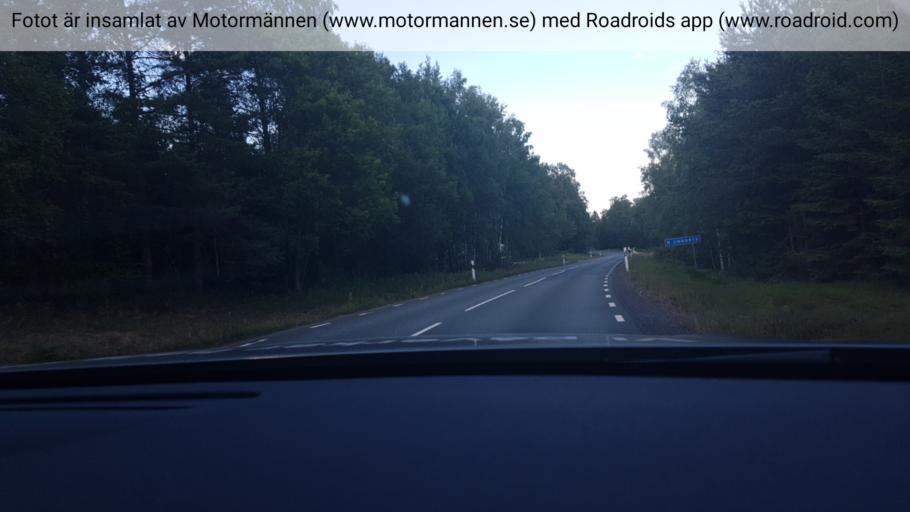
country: SE
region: Joenkoeping
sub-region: Gnosjo Kommun
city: Gnosjoe
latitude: 57.5955
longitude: 13.7014
